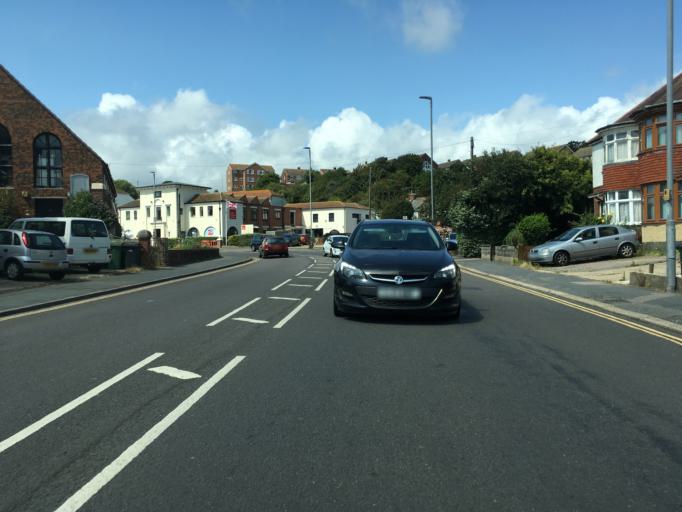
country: GB
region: England
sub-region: East Sussex
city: Saint Leonards-on-Sea
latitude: 50.8518
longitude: 0.5299
